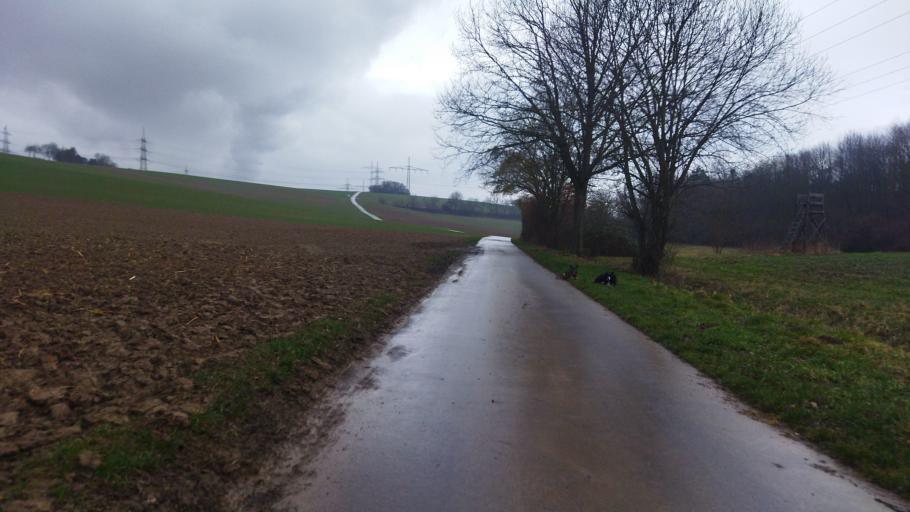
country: DE
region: Baden-Wuerttemberg
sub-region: Regierungsbezirk Stuttgart
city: Neckarwestheim
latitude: 49.0441
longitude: 9.2147
